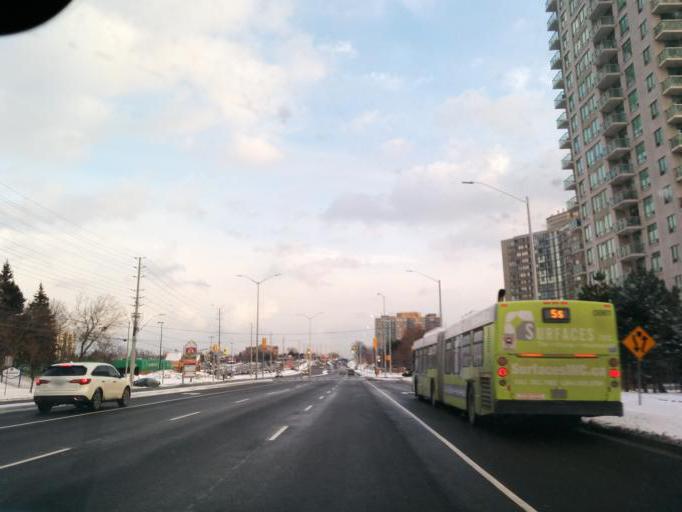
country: CA
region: Ontario
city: Etobicoke
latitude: 43.6267
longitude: -79.6086
